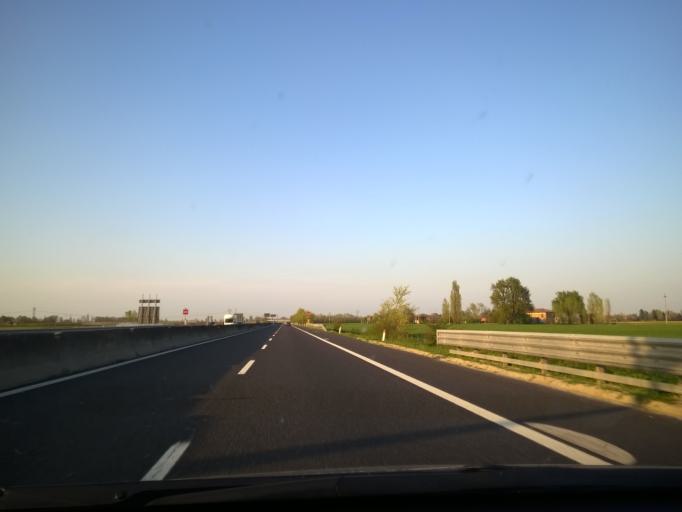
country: IT
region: Emilia-Romagna
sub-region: Provincia di Bologna
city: Bentivoglio
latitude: 44.5956
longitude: 11.4030
